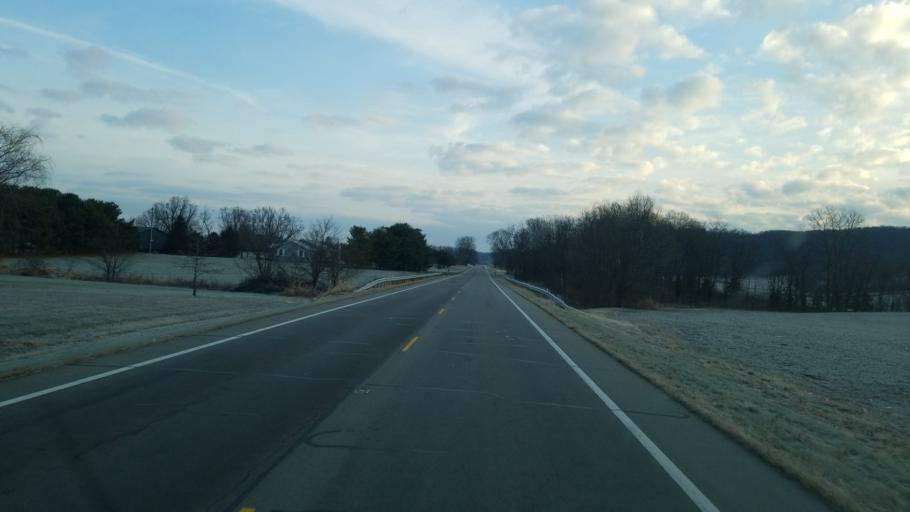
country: US
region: Ohio
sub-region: Ross County
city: North Fork Village
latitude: 39.3371
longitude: -83.0868
